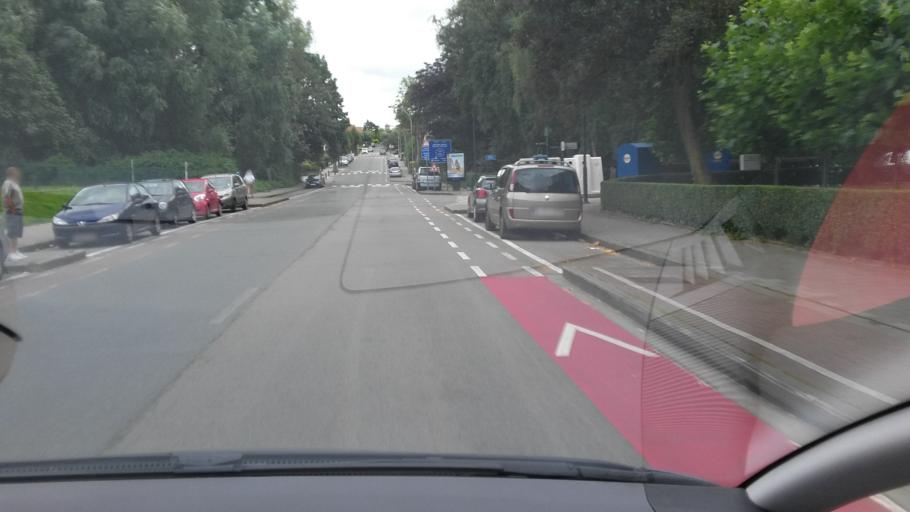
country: BE
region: Flanders
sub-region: Provincie Vlaams-Brabant
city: Hoeilaart
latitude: 50.8130
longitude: 4.4174
